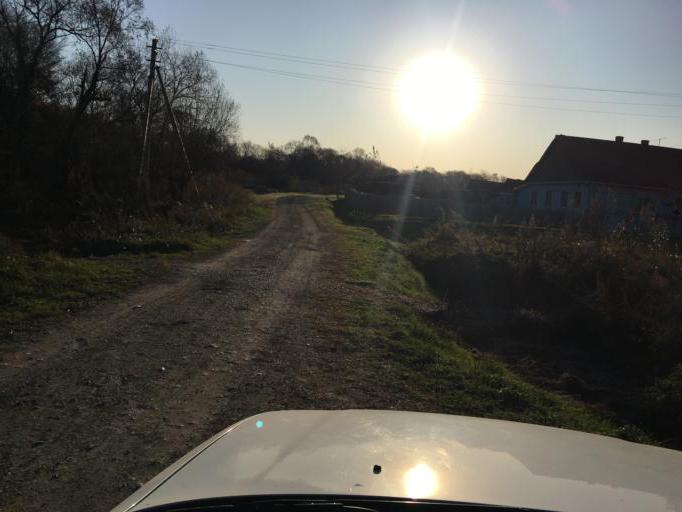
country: RU
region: Primorskiy
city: Lazo
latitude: 45.8631
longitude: 133.6454
